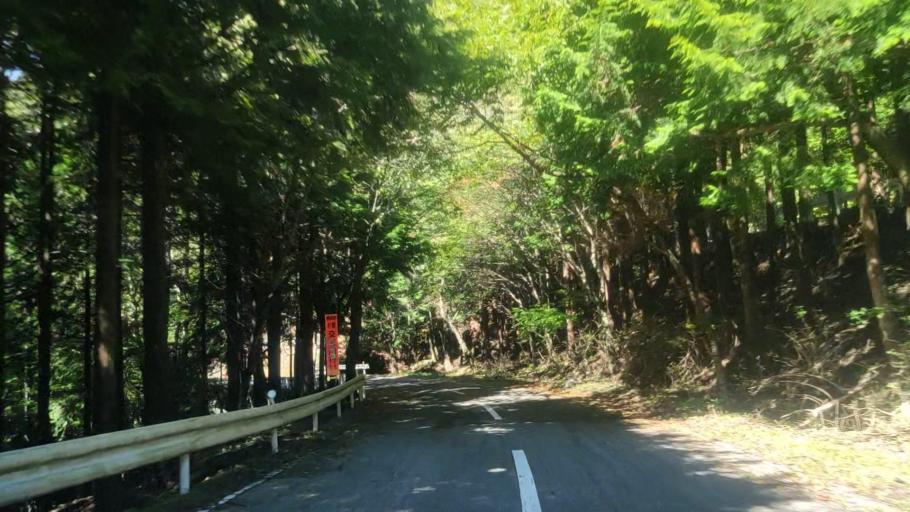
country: JP
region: Yamanashi
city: Fujikawaguchiko
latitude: 35.5683
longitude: 138.7852
